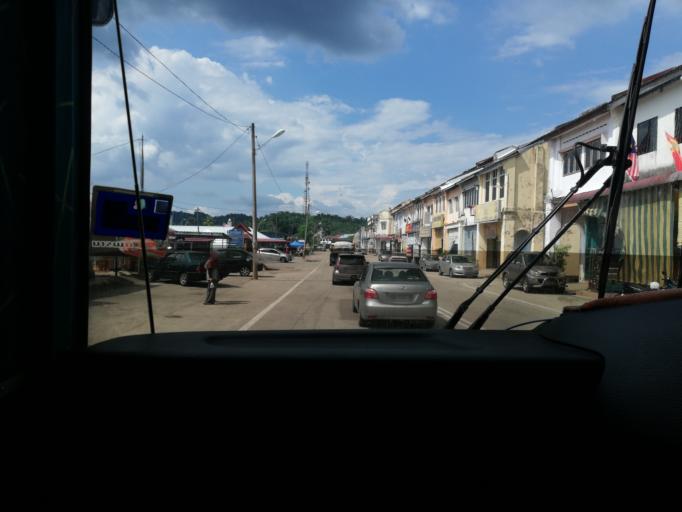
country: MY
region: Penang
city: Nibong Tebal
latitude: 5.2108
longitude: 100.6119
